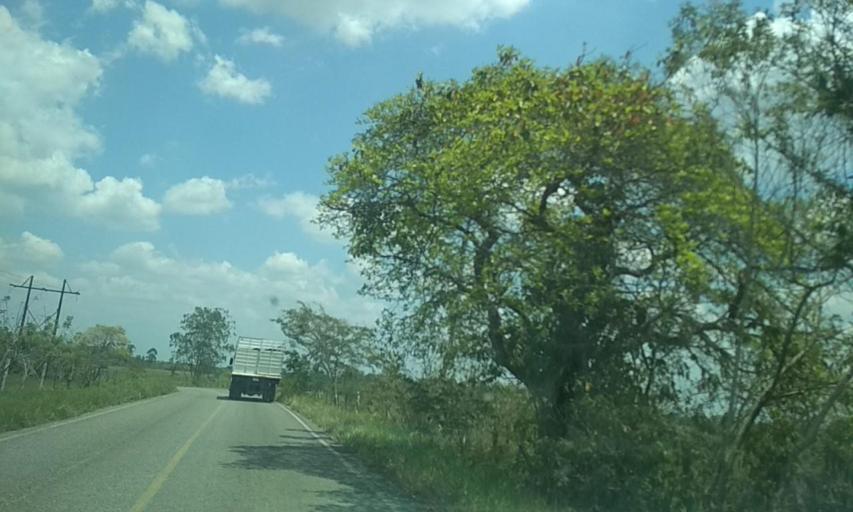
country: MX
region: Tabasco
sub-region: Huimanguillo
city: Francisco Rueda
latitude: 17.7682
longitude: -93.8008
